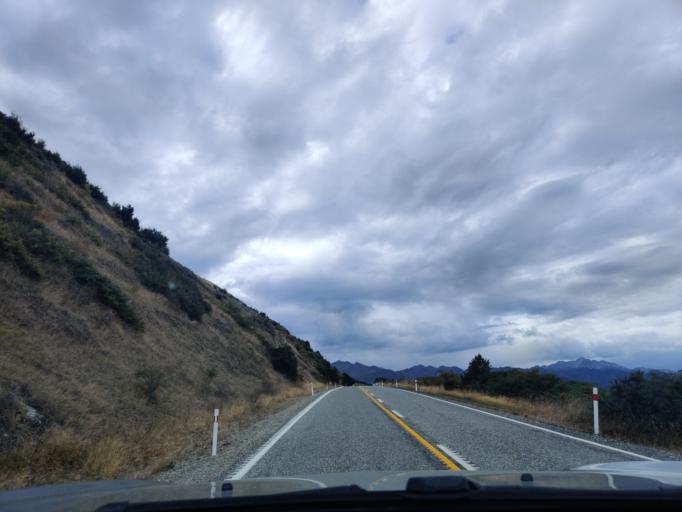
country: NZ
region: Otago
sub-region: Queenstown-Lakes District
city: Wanaka
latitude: -44.5124
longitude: 169.2470
